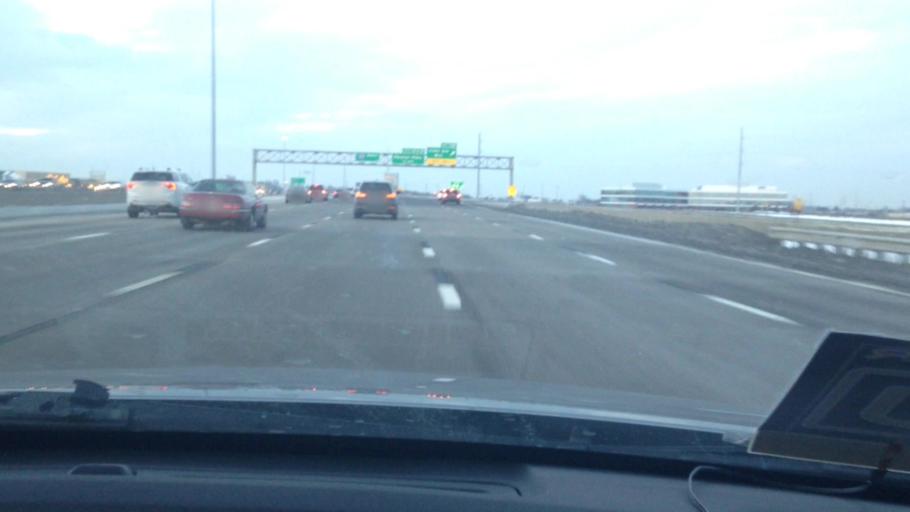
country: US
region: Kansas
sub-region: Wyandotte County
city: Edwardsville
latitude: 39.1159
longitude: -94.8117
